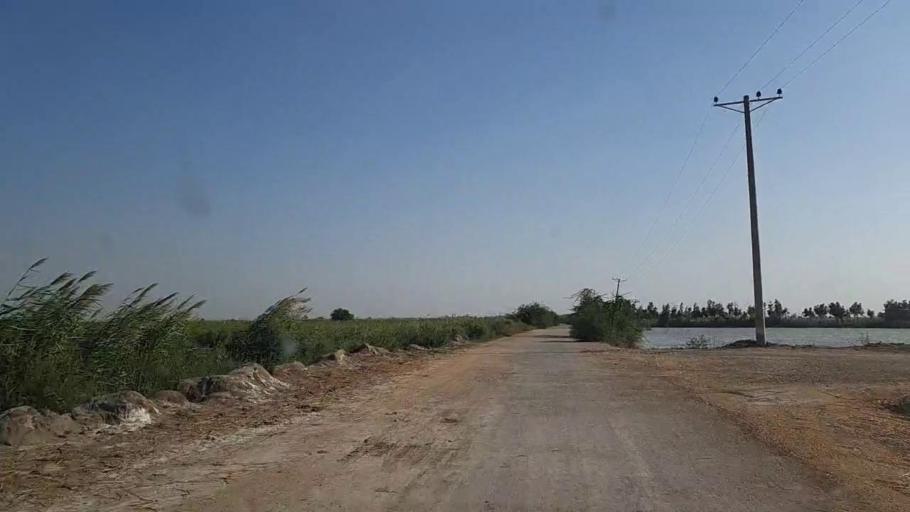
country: PK
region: Sindh
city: Thatta
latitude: 24.6402
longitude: 68.0756
